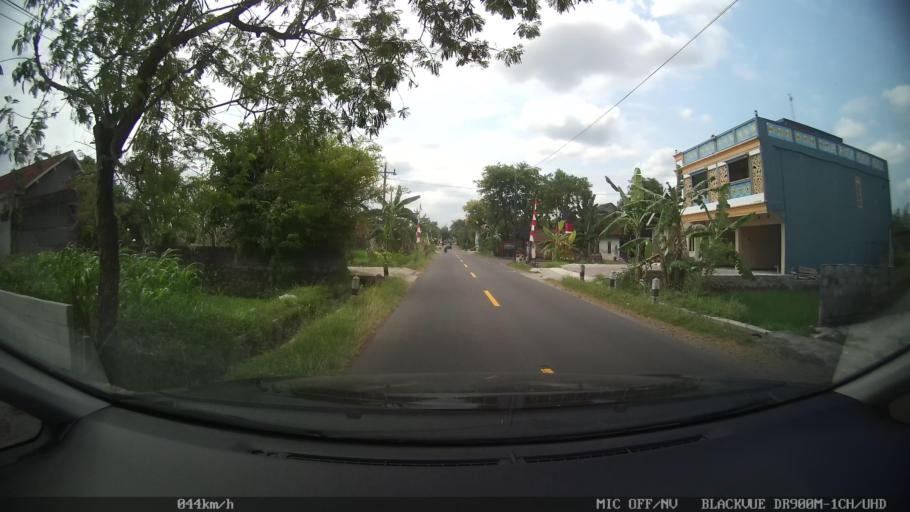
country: ID
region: Central Java
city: Candi Prambanan
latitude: -7.7471
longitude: 110.4812
